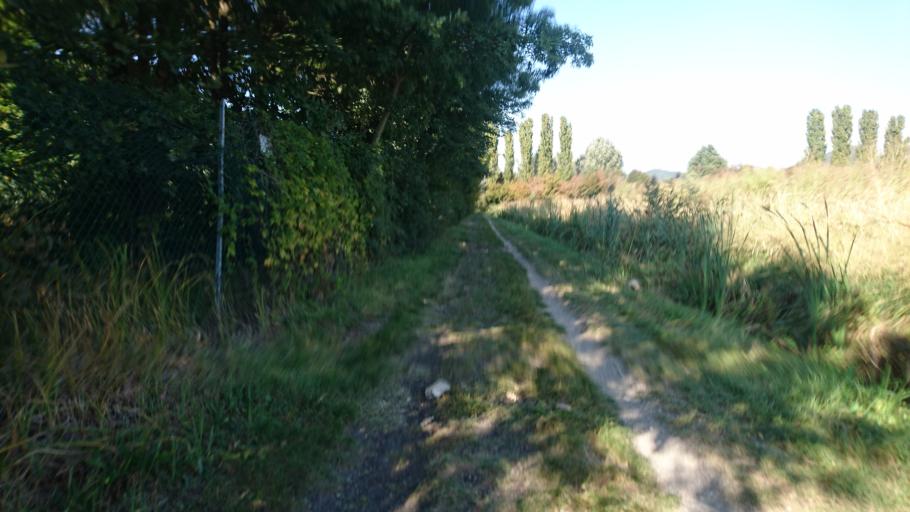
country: IT
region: Veneto
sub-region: Provincia di Padova
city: Galzignano
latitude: 45.2915
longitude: 11.7412
